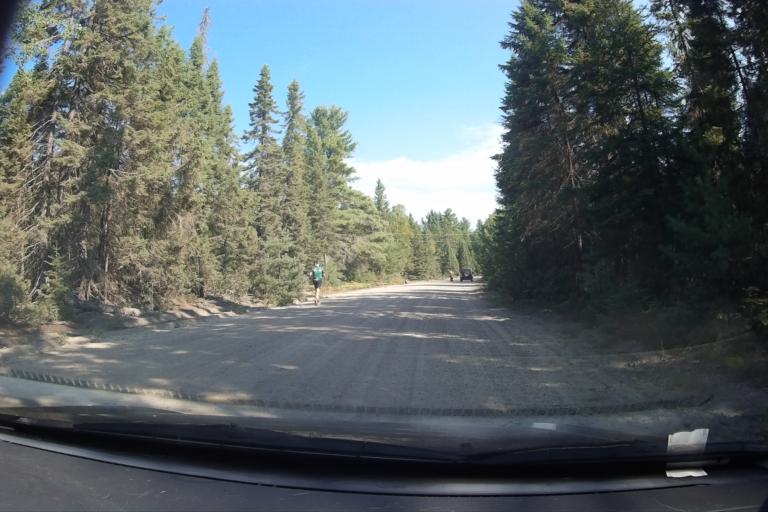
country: CA
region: Ontario
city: Huntsville
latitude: 45.5701
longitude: -78.7119
